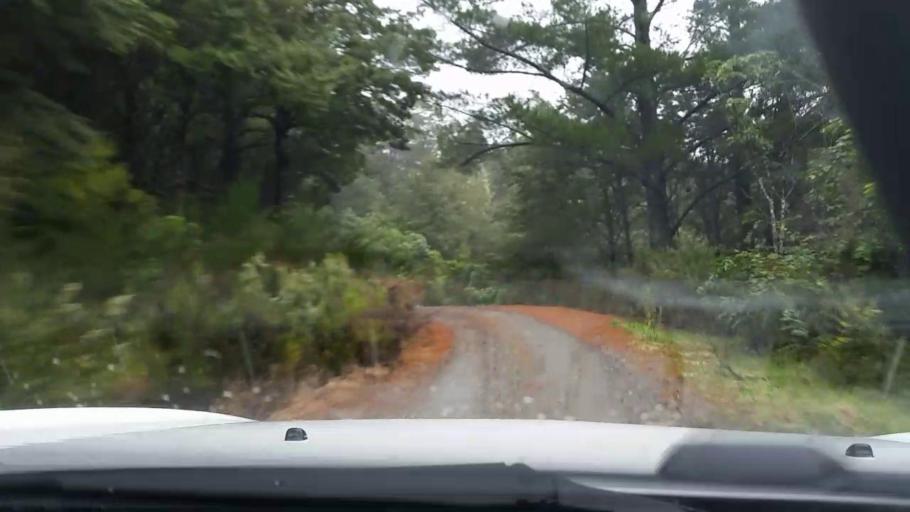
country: NZ
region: Wellington
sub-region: Masterton District
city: Masterton
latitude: -41.1584
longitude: 175.8026
